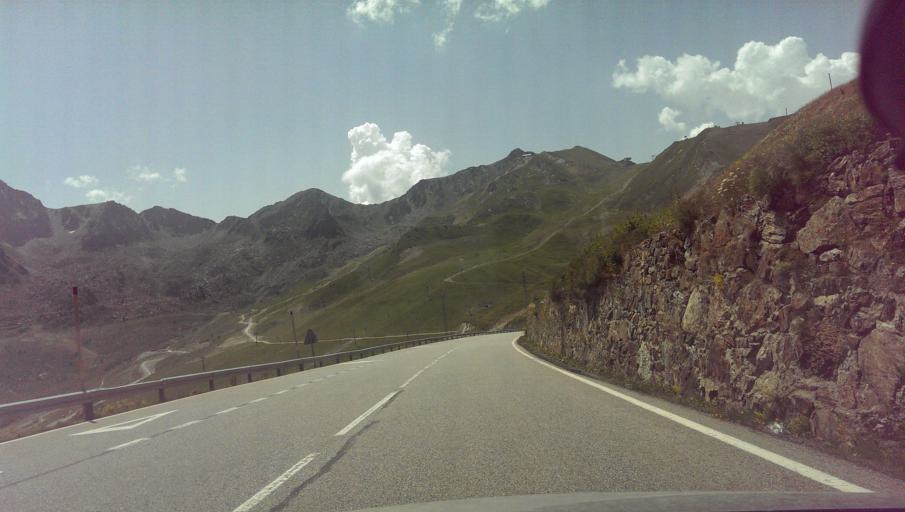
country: AD
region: Encamp
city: Pas de la Casa
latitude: 42.5428
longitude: 1.7279
